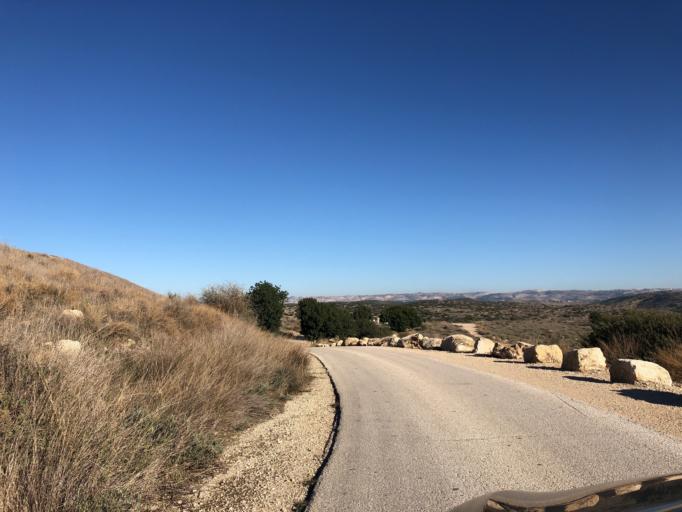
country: PS
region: West Bank
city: Idhna
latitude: 31.5919
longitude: 34.8978
